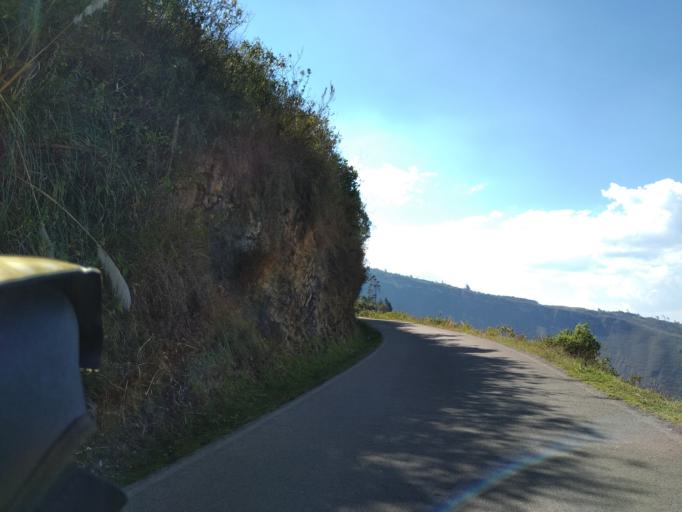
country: PE
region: Amazonas
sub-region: Provincia de Chachapoyas
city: Montevideo
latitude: -6.7206
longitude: -77.8046
